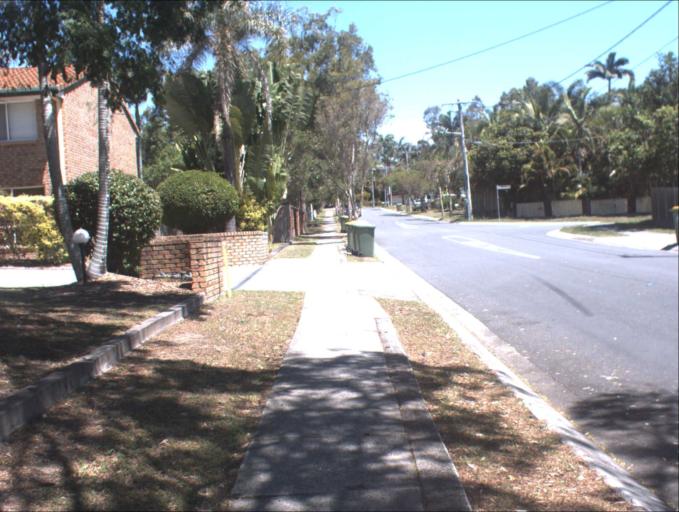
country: AU
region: Queensland
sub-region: Logan
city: Woodridge
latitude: -27.6229
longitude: 153.1071
